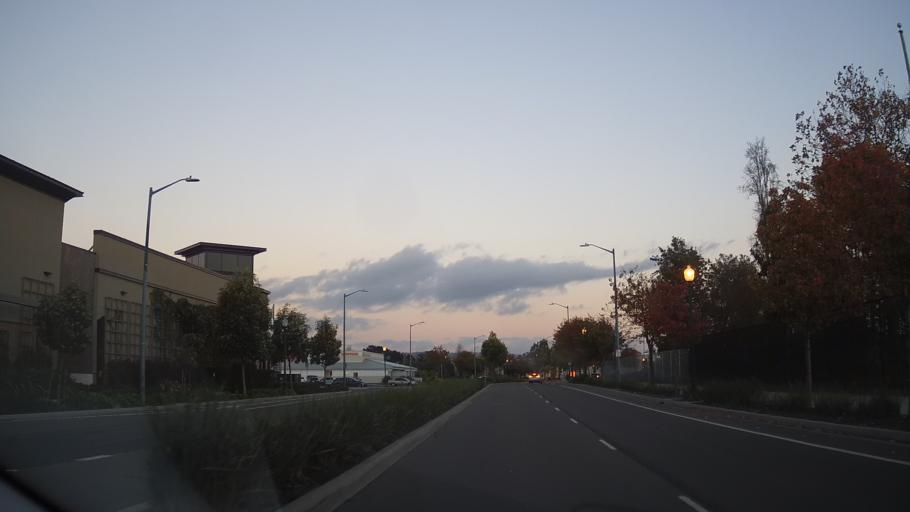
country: US
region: California
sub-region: Alameda County
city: Oakland
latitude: 37.7851
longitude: -122.2807
